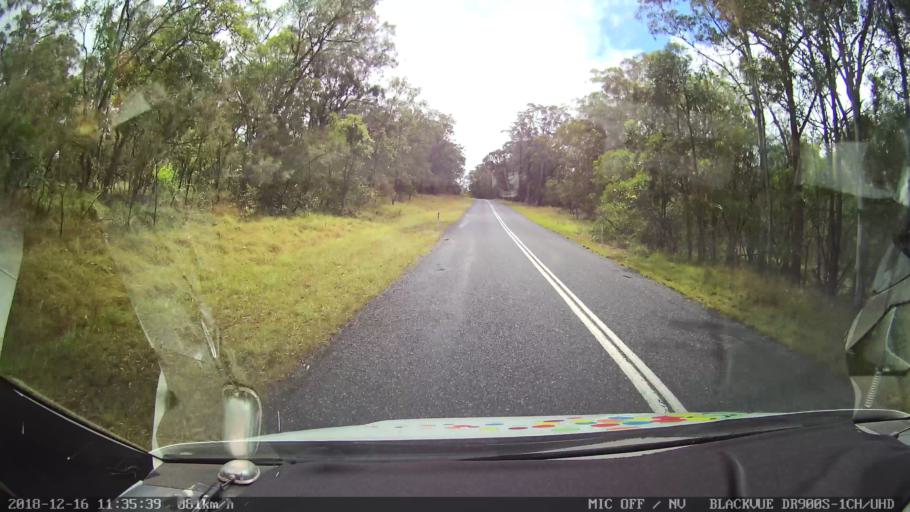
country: AU
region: New South Wales
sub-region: Tenterfield Municipality
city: Carrolls Creek
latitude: -28.9880
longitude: 152.1642
